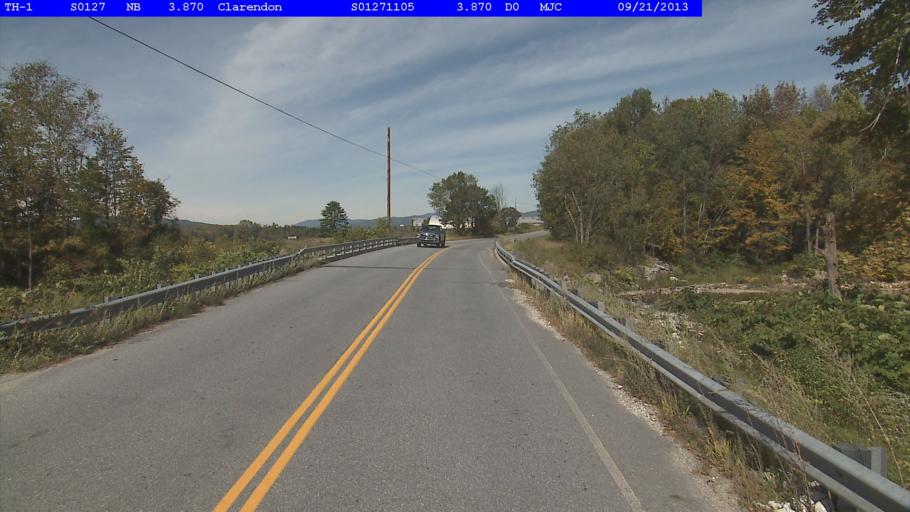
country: US
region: Vermont
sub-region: Rutland County
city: Rutland
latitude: 43.5690
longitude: -72.9720
